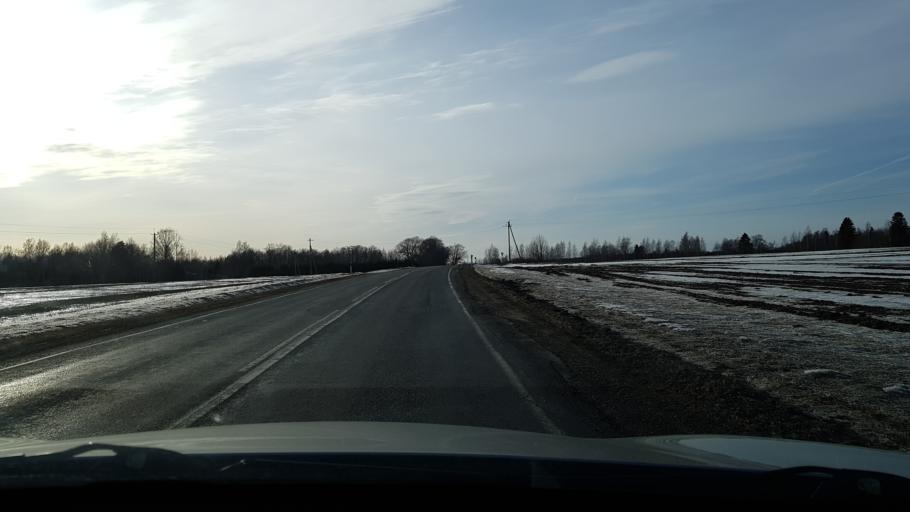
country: EE
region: Viljandimaa
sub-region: Suure-Jaani vald
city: Suure-Jaani
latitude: 58.3542
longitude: 25.3893
